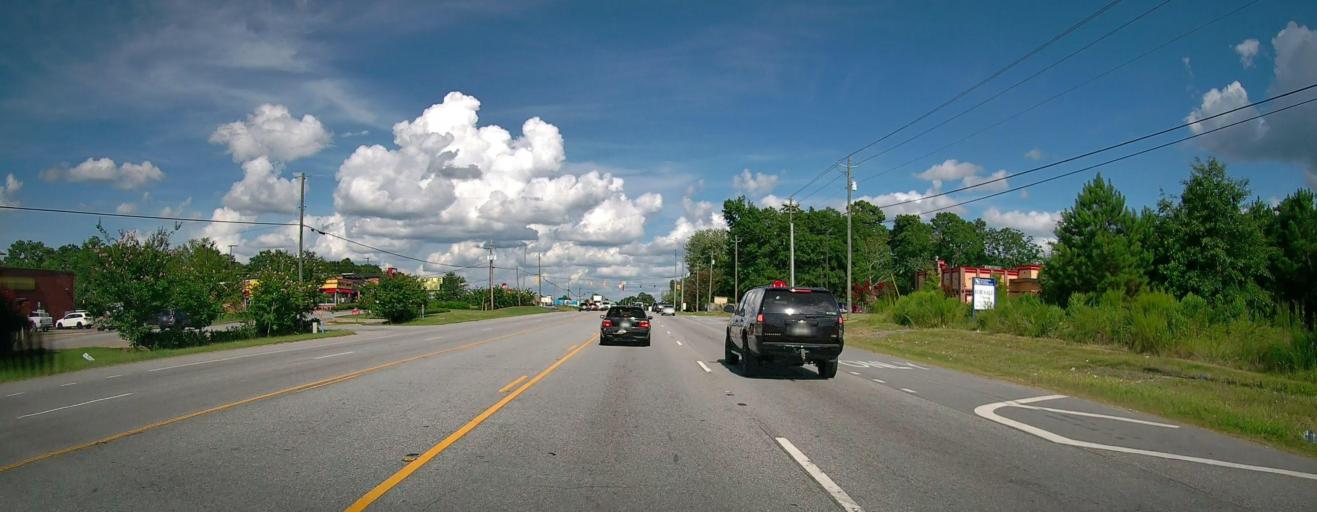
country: US
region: Alabama
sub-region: Russell County
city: Ladonia
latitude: 32.4700
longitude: -85.0912
